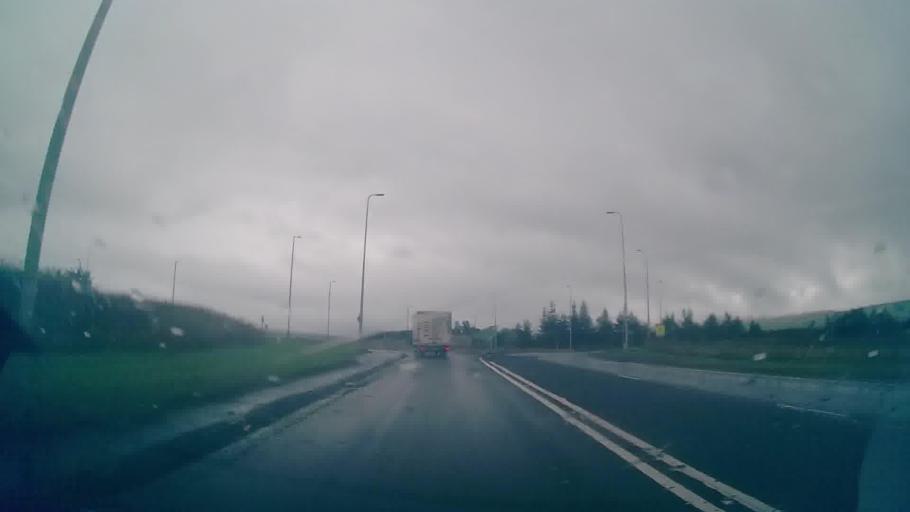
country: GB
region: Scotland
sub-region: East Ayrshire
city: New Cumnock
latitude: 55.4058
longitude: -4.1927
